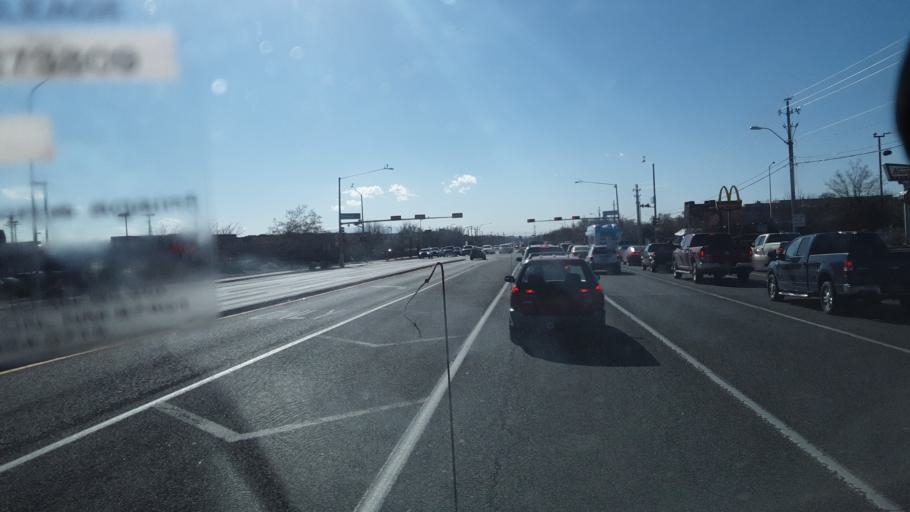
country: US
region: New Mexico
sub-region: Santa Fe County
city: Agua Fria
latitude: 35.6505
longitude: -106.0001
